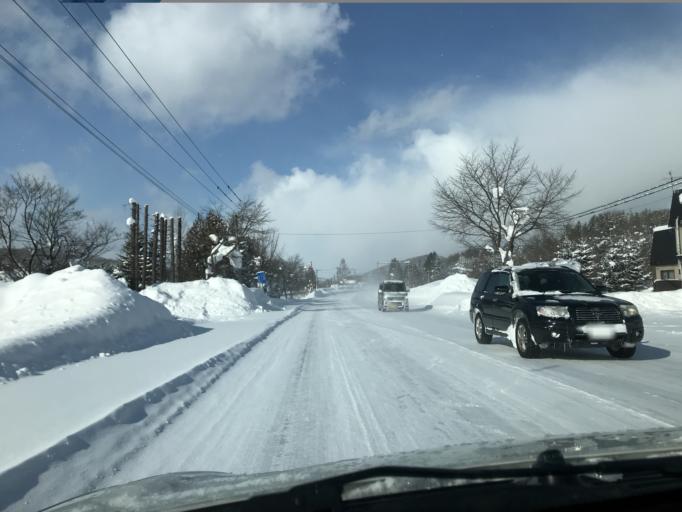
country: JP
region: Hokkaido
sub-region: Asahikawa-shi
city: Asahikawa
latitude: 43.9259
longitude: 142.4749
